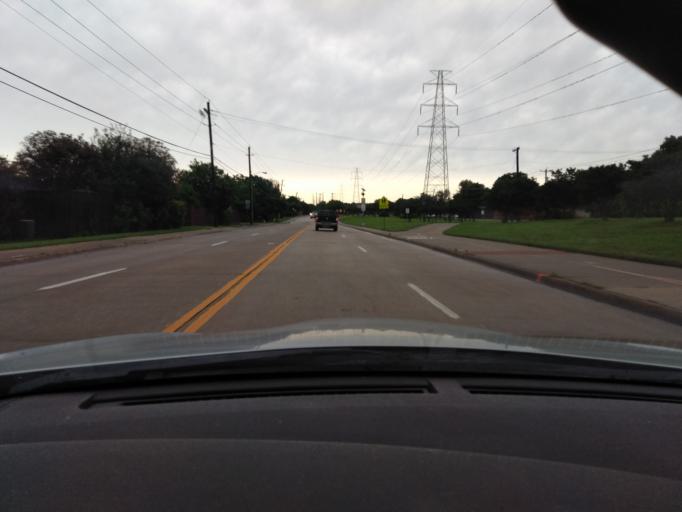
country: US
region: Texas
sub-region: Dallas County
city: Addison
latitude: 32.9687
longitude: -96.7785
